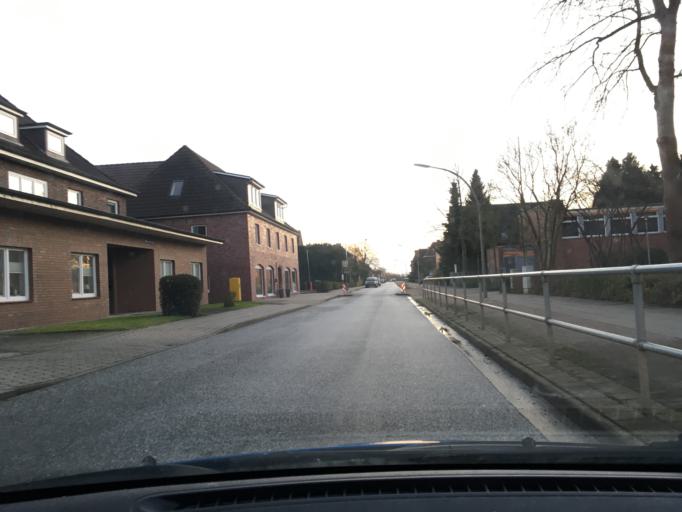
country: DE
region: Lower Saxony
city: Neu Wulmstorf
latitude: 53.5164
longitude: 9.8113
